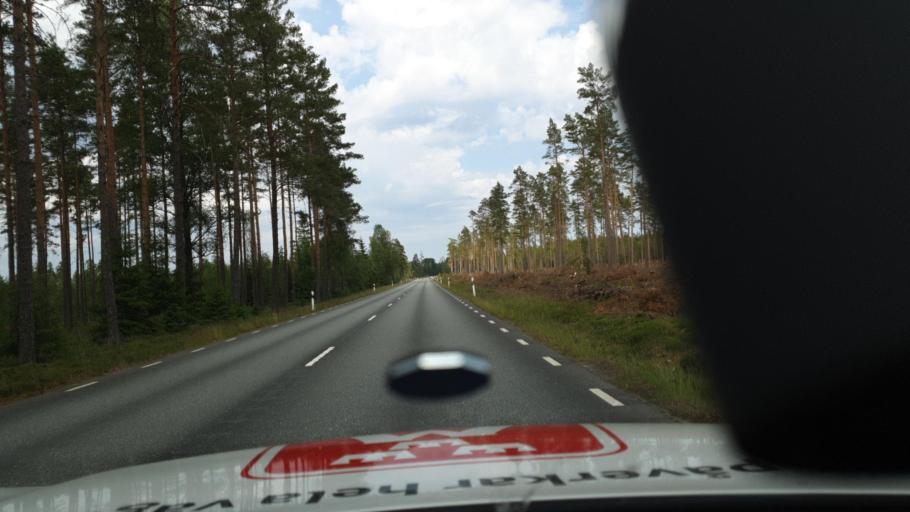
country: SE
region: Joenkoeping
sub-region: Varnamo Kommun
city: Varnamo
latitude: 57.2900
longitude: 14.0726
